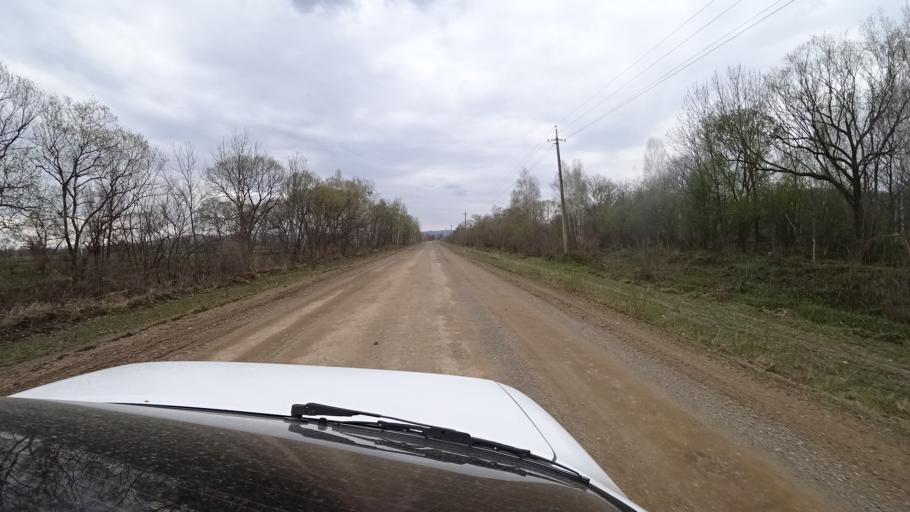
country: RU
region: Primorskiy
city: Novopokrovka
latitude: 45.5600
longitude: 134.3438
